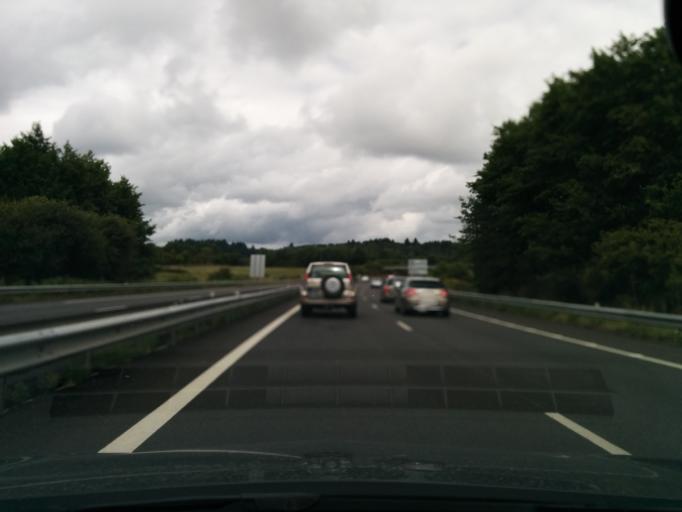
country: FR
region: Limousin
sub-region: Departement de la Haute-Vienne
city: Razes
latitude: 46.0137
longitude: 1.3387
